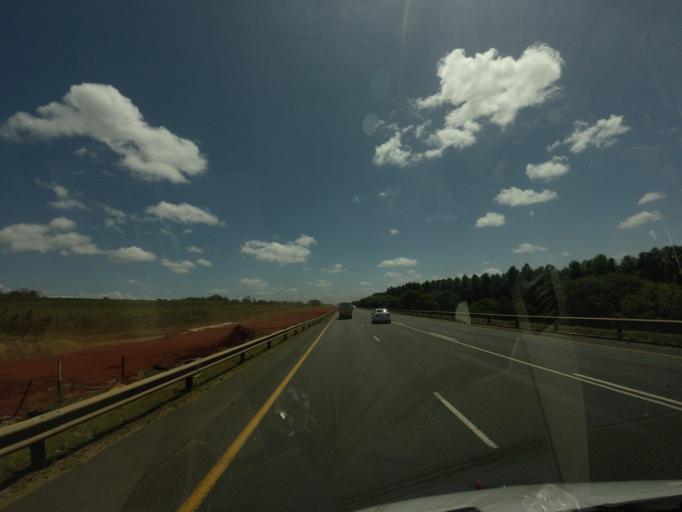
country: ZA
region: KwaZulu-Natal
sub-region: uThungulu District Municipality
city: Empangeni
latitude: -28.8108
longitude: 31.9154
